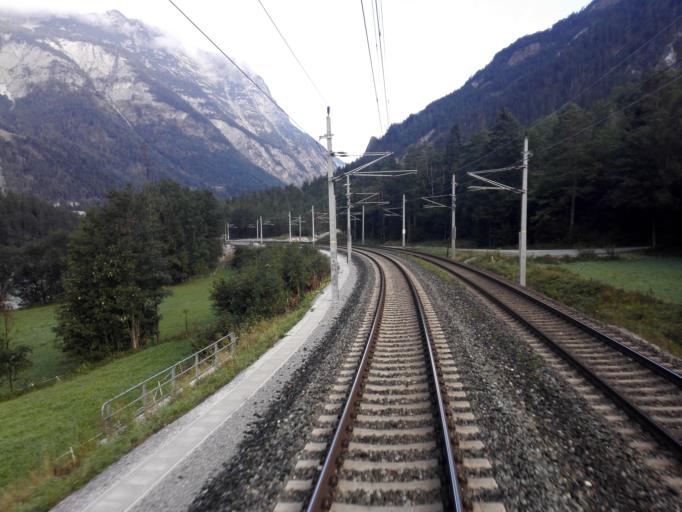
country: AT
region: Salzburg
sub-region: Politischer Bezirk Sankt Johann im Pongau
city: Werfen
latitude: 47.5098
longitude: 13.1710
